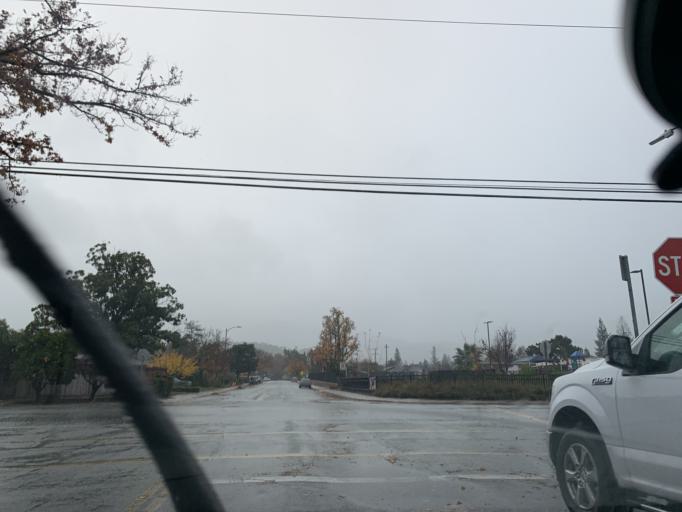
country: US
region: California
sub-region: Santa Clara County
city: Cambrian Park
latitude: 37.2485
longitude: -121.9449
